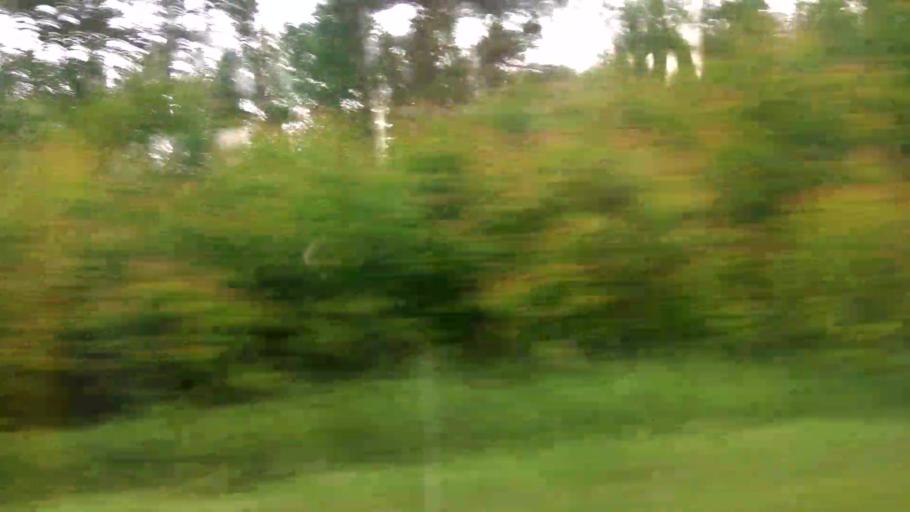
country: RU
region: Moskovskaya
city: Zaraysk
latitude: 54.7691
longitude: 38.8229
